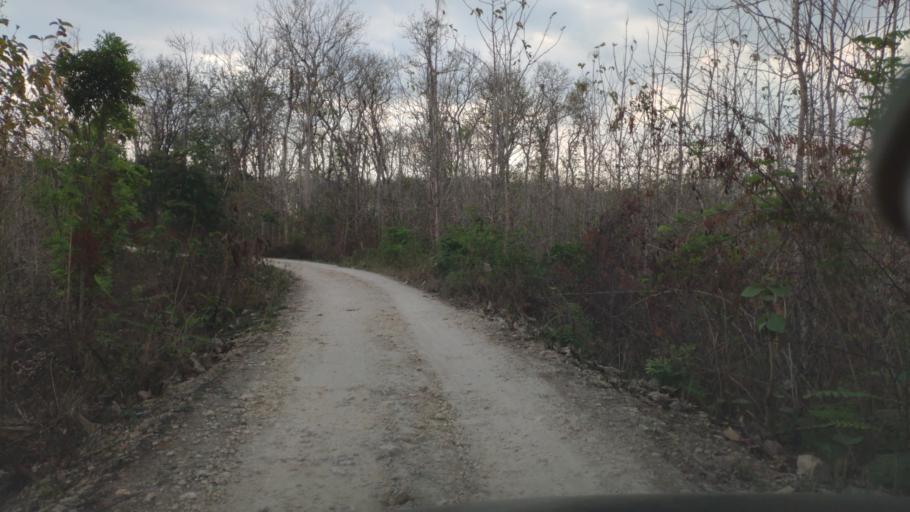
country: ID
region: Central Java
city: Randublatung
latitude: -7.2874
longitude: 111.3000
